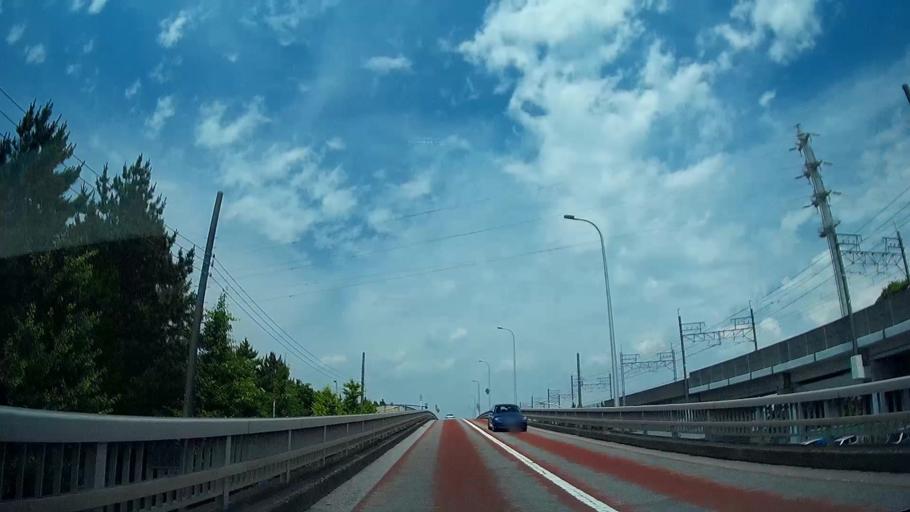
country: JP
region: Tokyo
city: Urayasu
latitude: 35.6548
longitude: 139.9172
